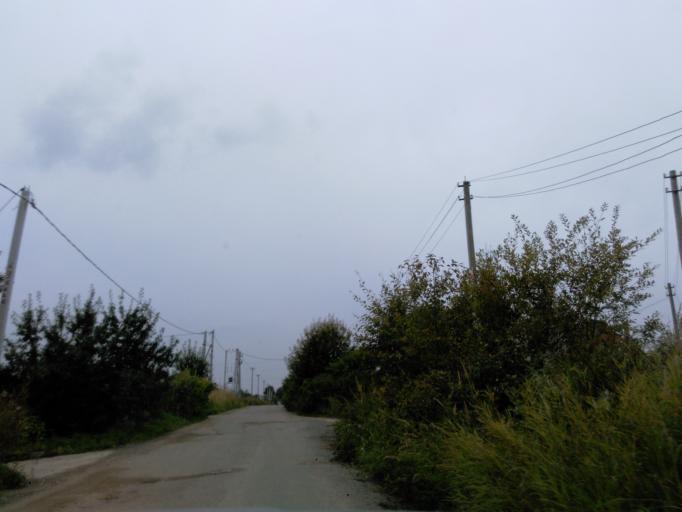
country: RU
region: Moskovskaya
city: Lozhki
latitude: 56.0641
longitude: 37.1013
